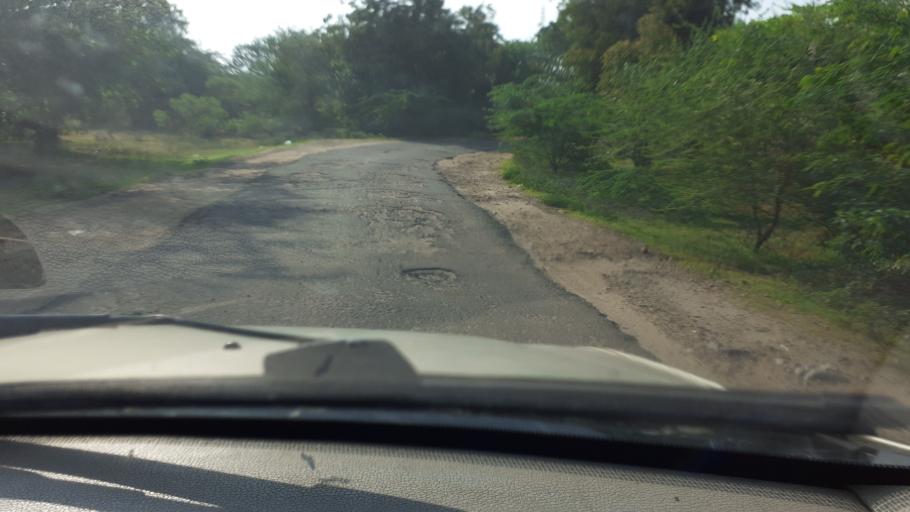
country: IN
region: Tamil Nadu
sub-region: Thoothukkudi
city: Eral
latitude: 8.5729
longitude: 78.0194
